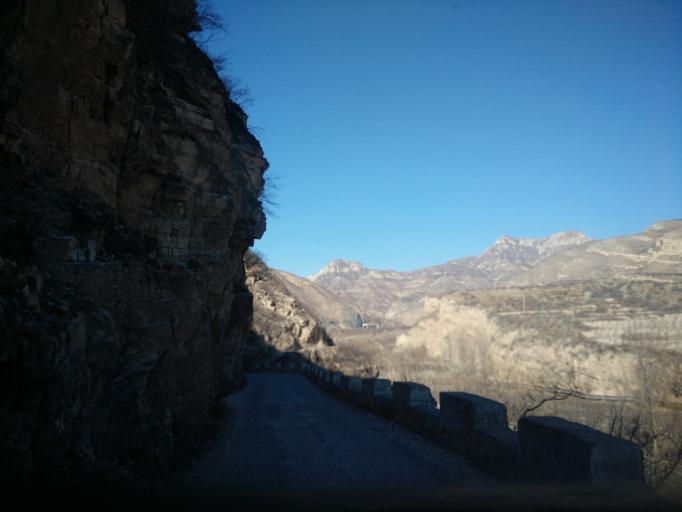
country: CN
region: Beijing
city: Zhaitang
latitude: 40.1585
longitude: 115.6765
